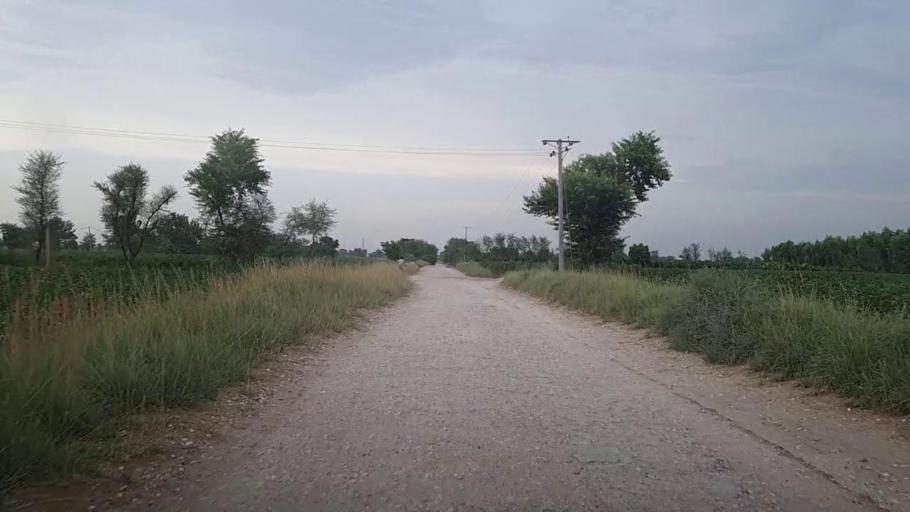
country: PK
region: Sindh
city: Karaundi
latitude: 26.9763
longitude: 68.3438
